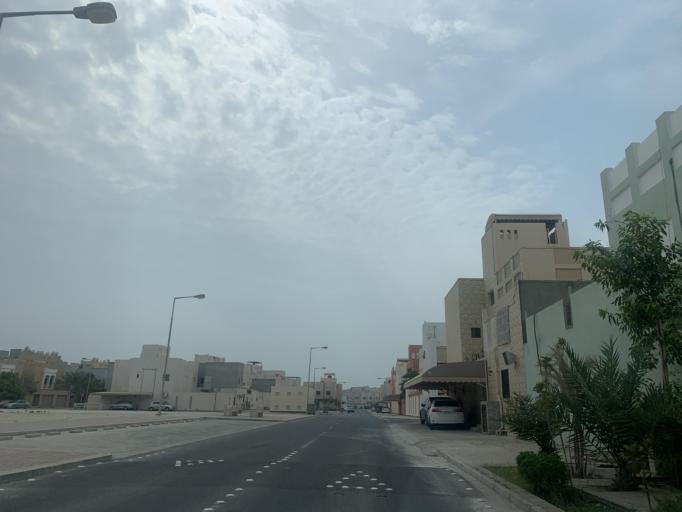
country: BH
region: Muharraq
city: Al Muharraq
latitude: 26.2840
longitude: 50.6396
